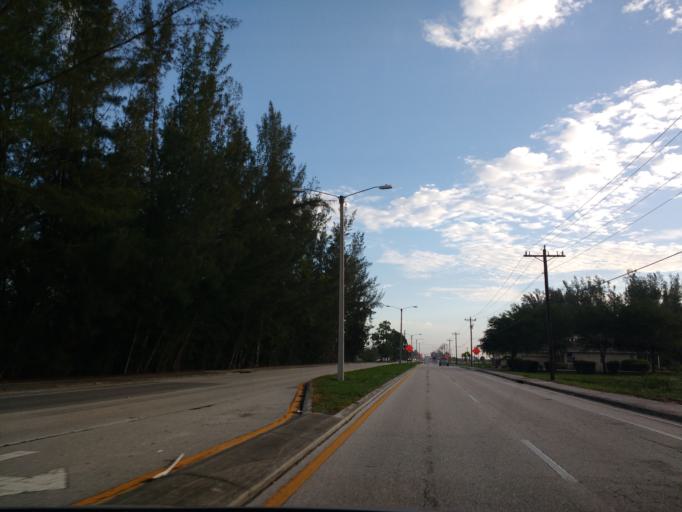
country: US
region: Florida
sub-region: Lee County
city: Cape Coral
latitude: 26.6333
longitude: -82.0071
